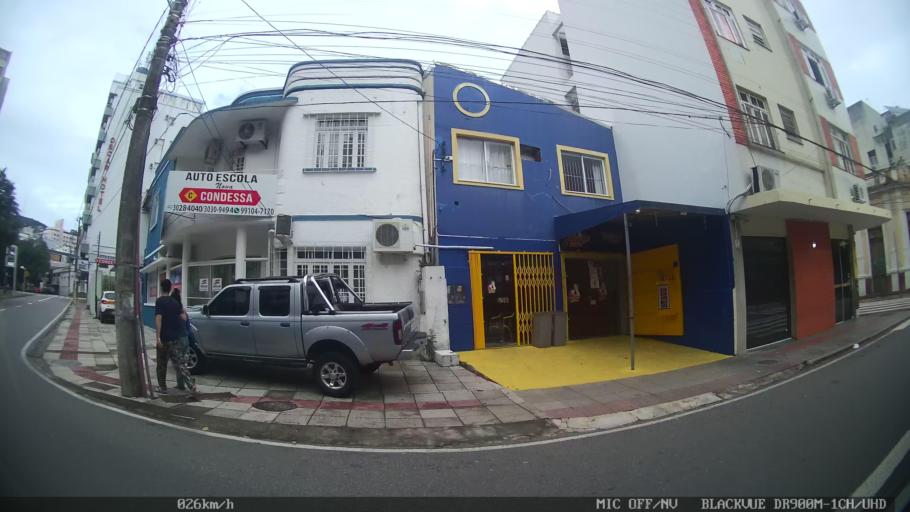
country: BR
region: Santa Catarina
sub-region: Florianopolis
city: Florianopolis
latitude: -27.5970
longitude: -48.5472
